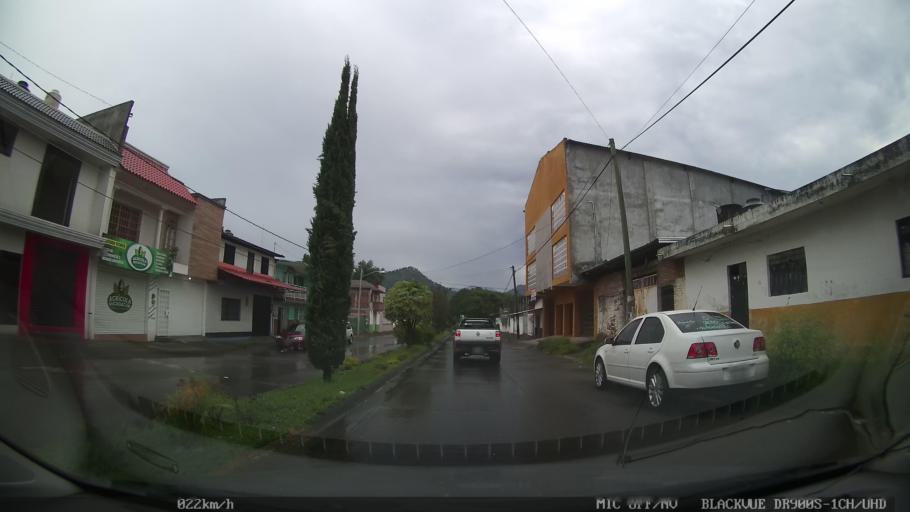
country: MX
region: Michoacan
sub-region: Uruapan
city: Santa Rosa (Santa Barbara)
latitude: 19.3891
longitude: -102.0550
